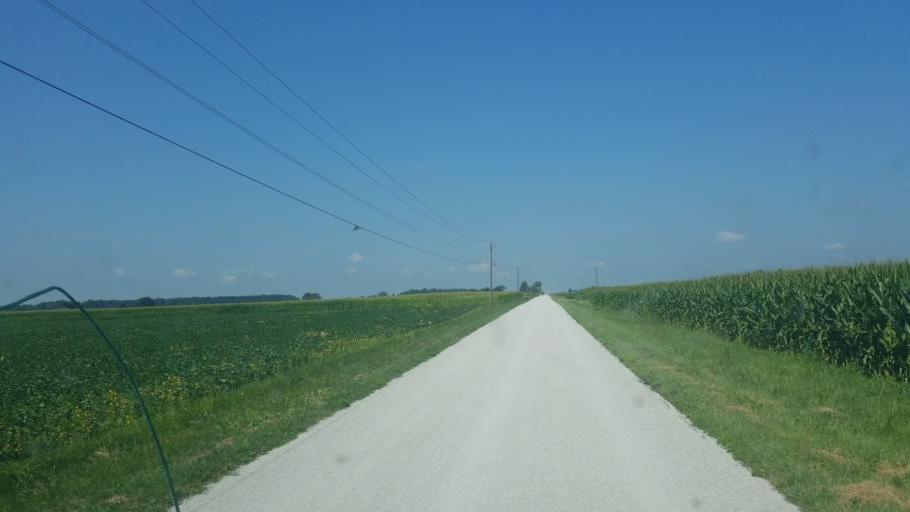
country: US
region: Ohio
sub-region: Hardin County
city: Kenton
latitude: 40.7032
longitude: -83.6640
